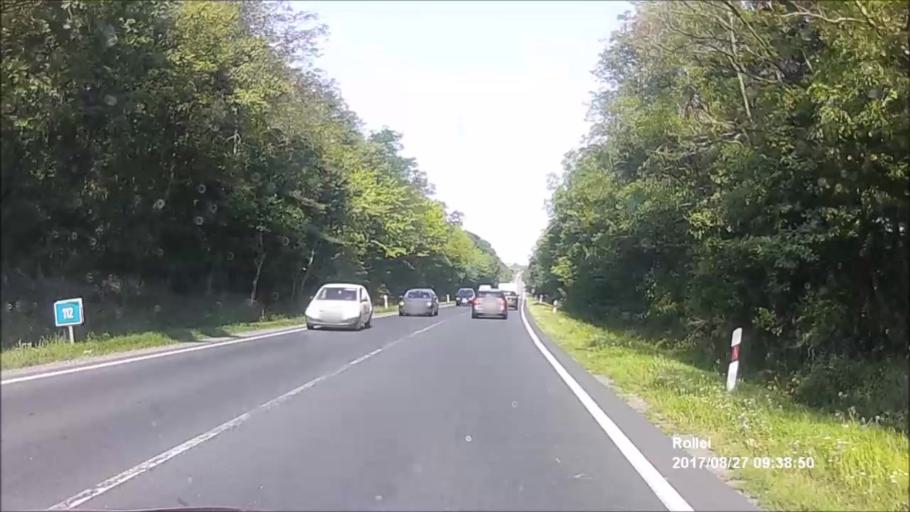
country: HU
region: Gyor-Moson-Sopron
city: Nagycenk
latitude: 47.6249
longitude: 16.6666
